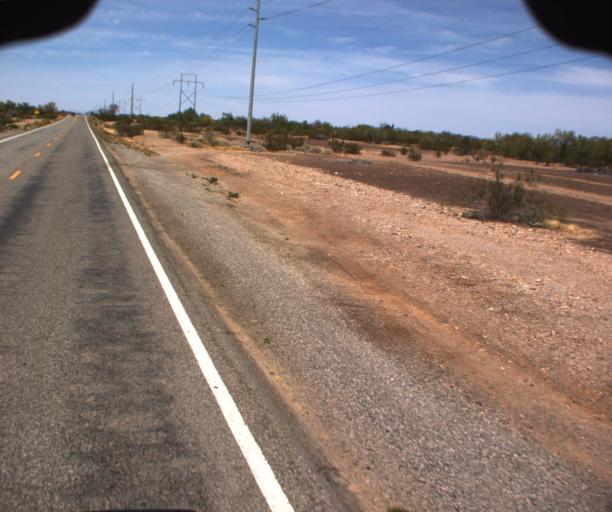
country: US
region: Arizona
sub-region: La Paz County
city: Quartzsite
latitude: 33.7429
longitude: -114.2170
